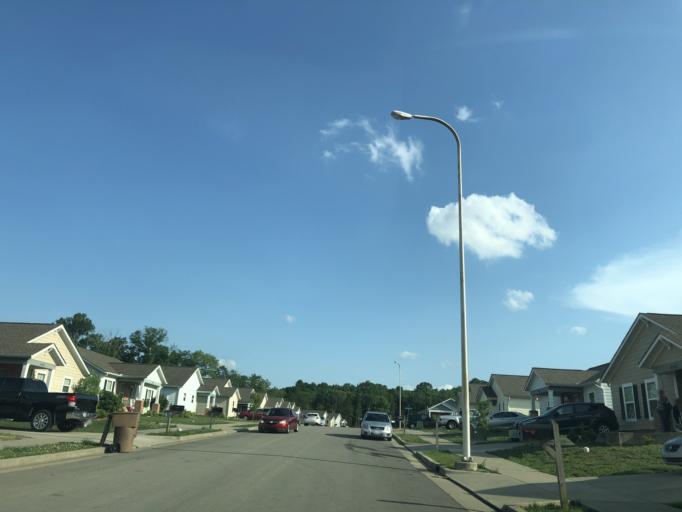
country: US
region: Tennessee
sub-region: Davidson County
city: Nashville
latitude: 36.2282
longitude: -86.7934
